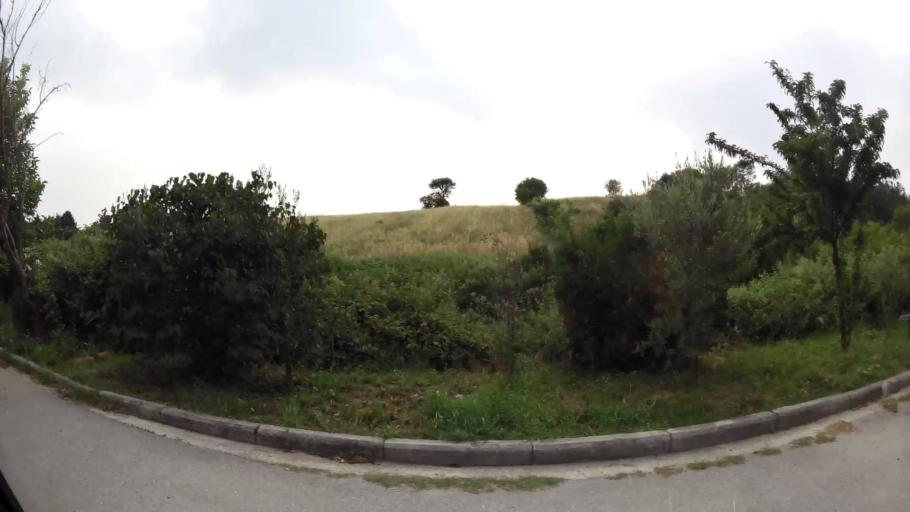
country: GR
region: Central Macedonia
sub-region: Nomos Thessalonikis
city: Oraiokastro
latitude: 40.7136
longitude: 22.9225
